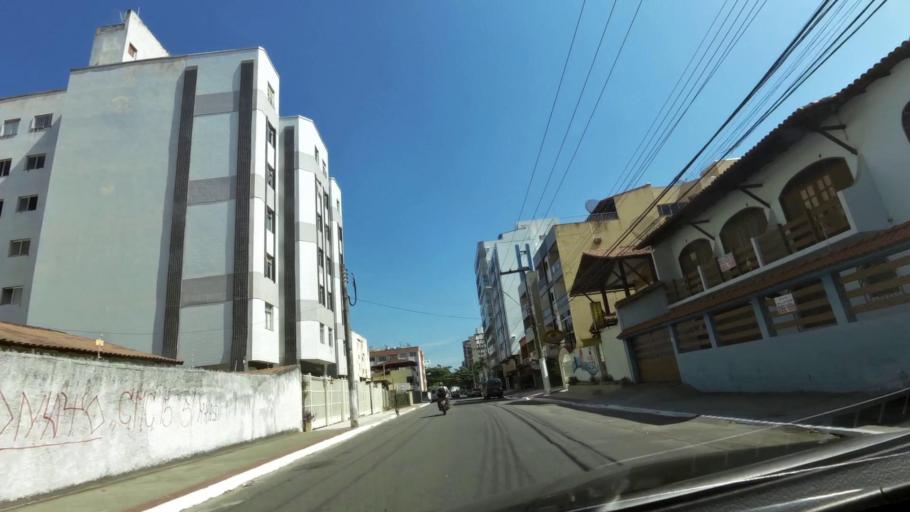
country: BR
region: Espirito Santo
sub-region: Guarapari
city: Guarapari
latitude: -20.6552
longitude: -40.4919
